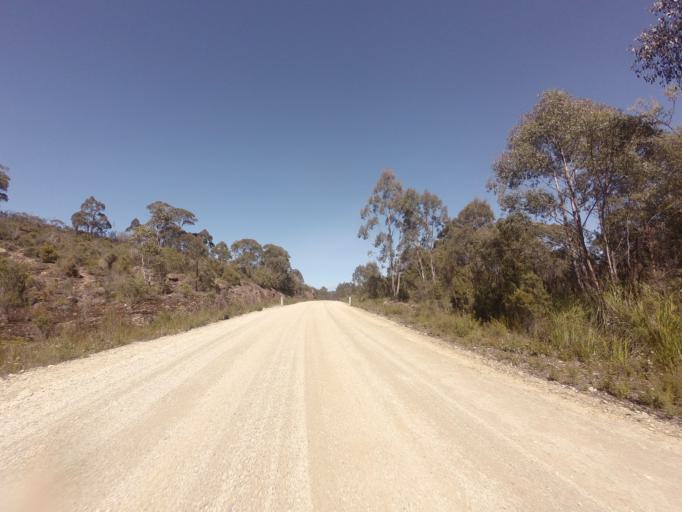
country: AU
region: Tasmania
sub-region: Huon Valley
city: Geeveston
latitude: -42.9062
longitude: 146.3688
